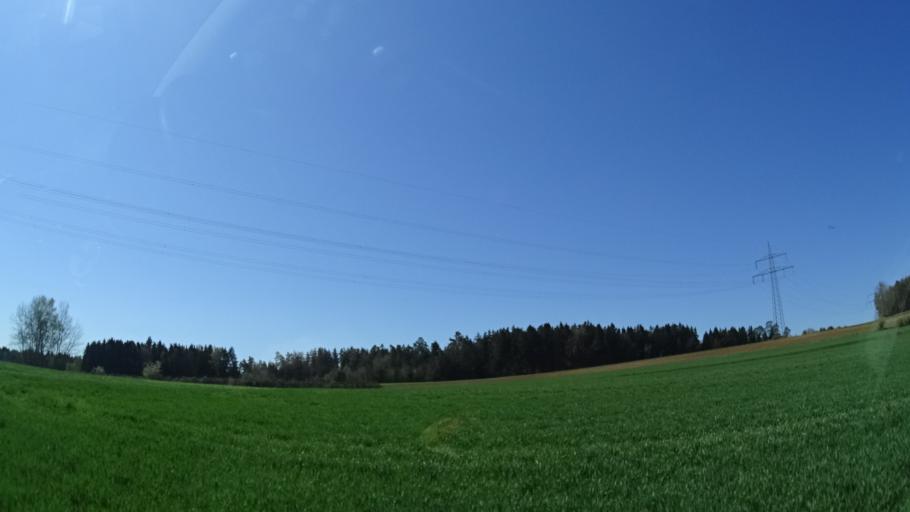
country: DE
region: Bavaria
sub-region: Upper Palatinate
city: Kastl
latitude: 49.4023
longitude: 11.6687
